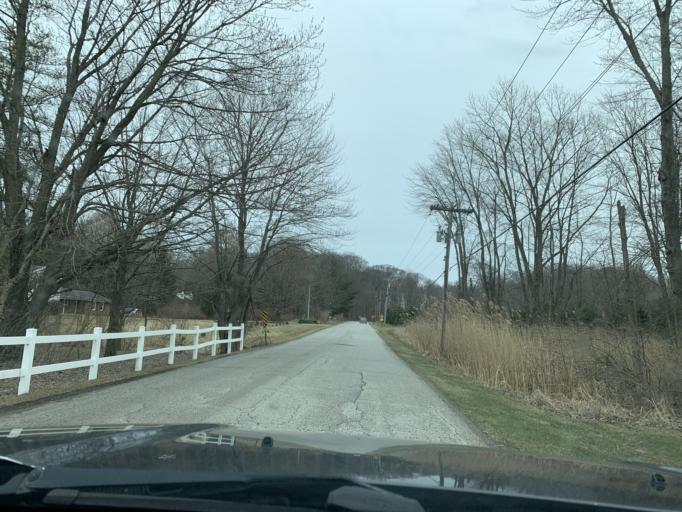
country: US
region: Indiana
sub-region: Porter County
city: Chesterton
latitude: 41.5856
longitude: -86.9921
